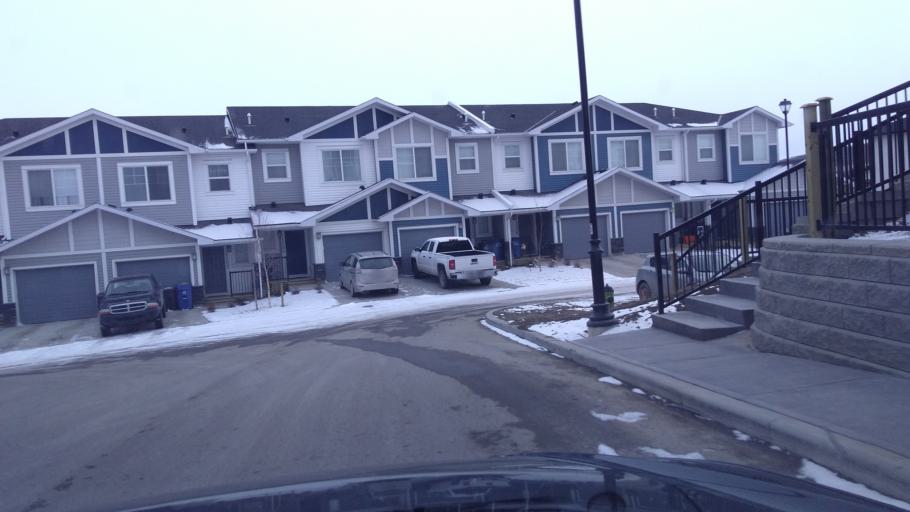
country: CA
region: Alberta
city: Cochrane
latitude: 51.1828
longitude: -114.5111
